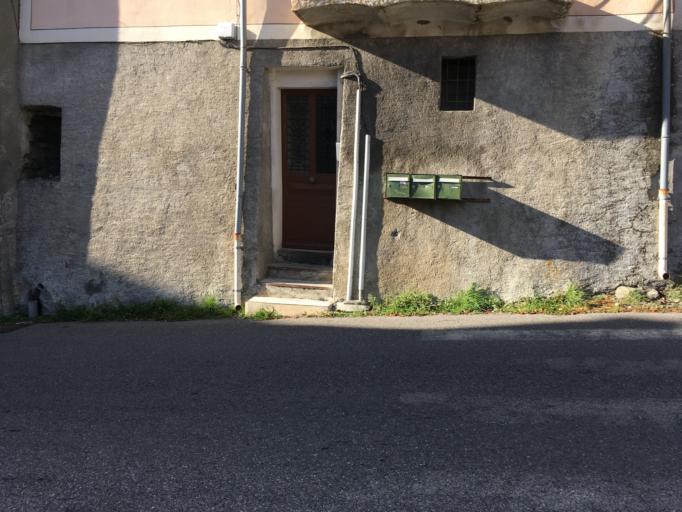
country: FR
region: Provence-Alpes-Cote d'Azur
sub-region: Departement des Alpes-de-Haute-Provence
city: Seyne-les-Alpes
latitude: 44.3505
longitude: 6.3568
